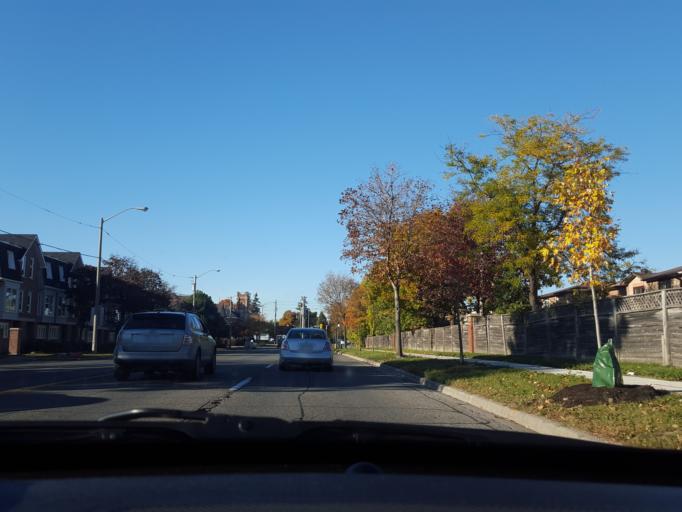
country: CA
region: Ontario
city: Markham
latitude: 43.8262
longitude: -79.2865
